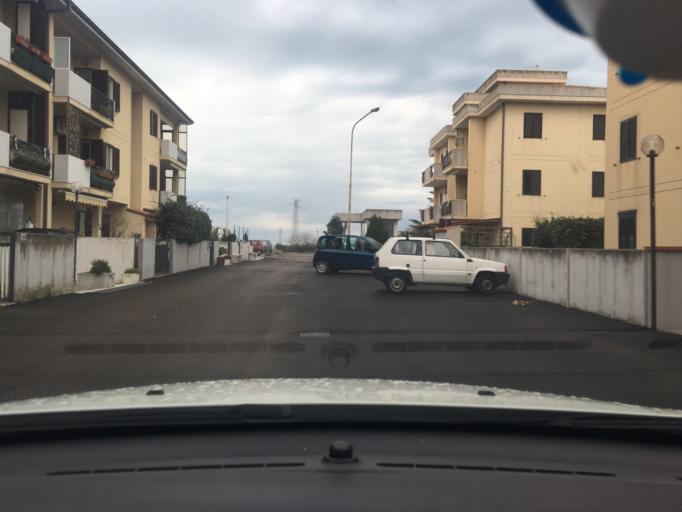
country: IT
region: Molise
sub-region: Provincia di Campobasso
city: Termoli
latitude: 41.9738
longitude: 14.9960
